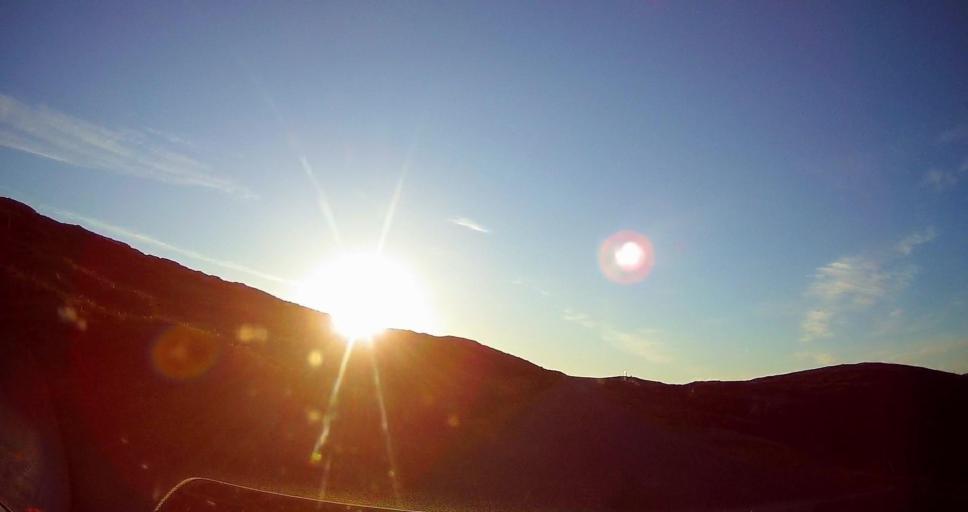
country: GB
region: Scotland
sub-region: Shetland Islands
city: Lerwick
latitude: 60.4409
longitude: -1.4013
